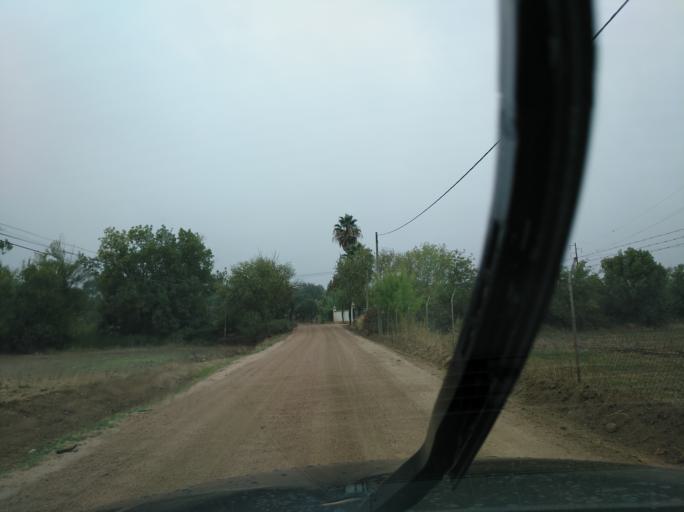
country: PT
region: Portalegre
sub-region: Campo Maior
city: Campo Maior
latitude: 38.9521
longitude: -7.0710
